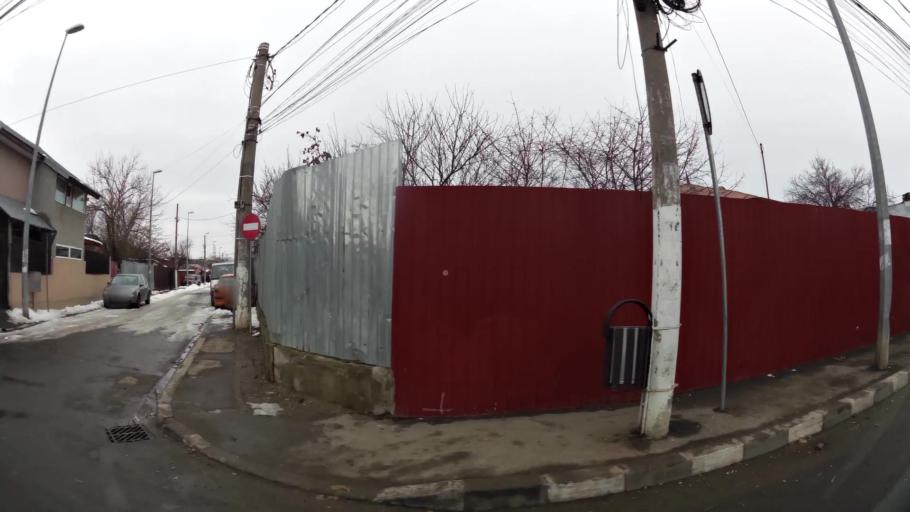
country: RO
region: Ilfov
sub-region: Comuna Pantelimon
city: Pantelimon
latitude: 44.4589
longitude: 26.2041
